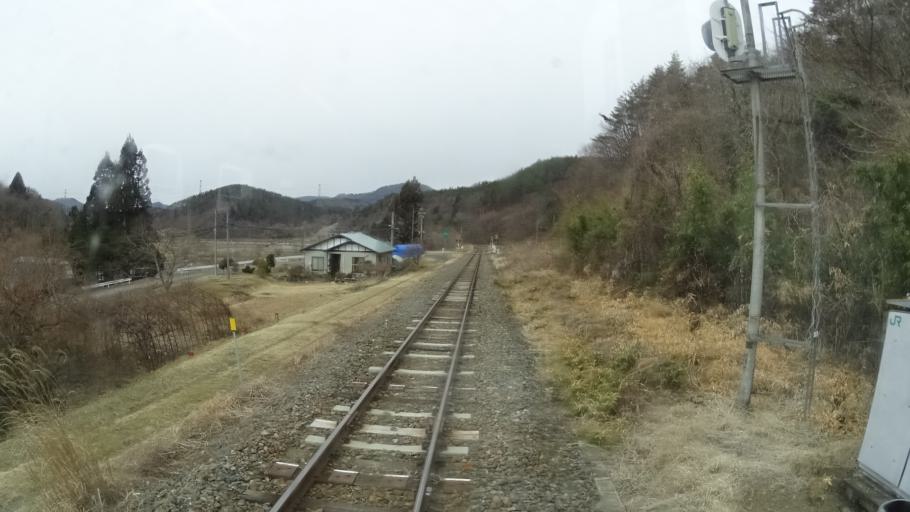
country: JP
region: Iwate
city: Tono
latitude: 39.3533
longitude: 141.3487
